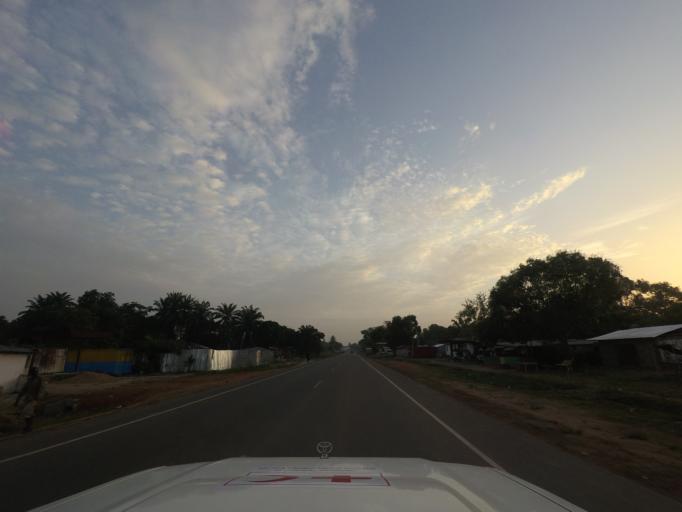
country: LR
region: Montserrado
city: Bensonville City
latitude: 6.3406
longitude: -10.6586
